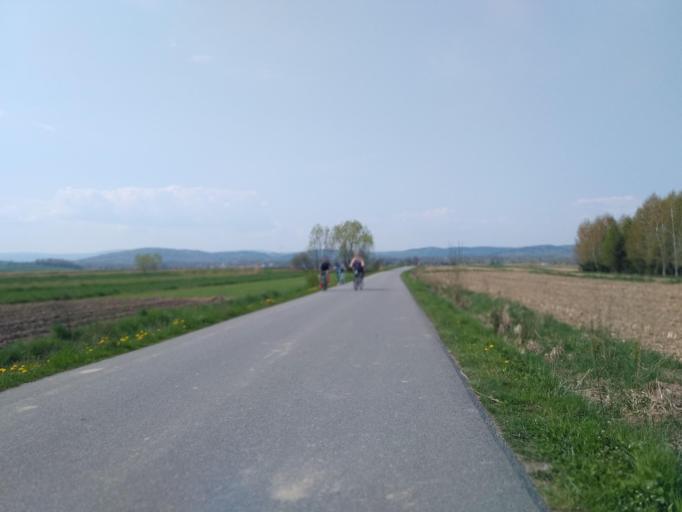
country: PL
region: Subcarpathian Voivodeship
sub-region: Krosno
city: Krosno
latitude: 49.6540
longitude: 21.7427
